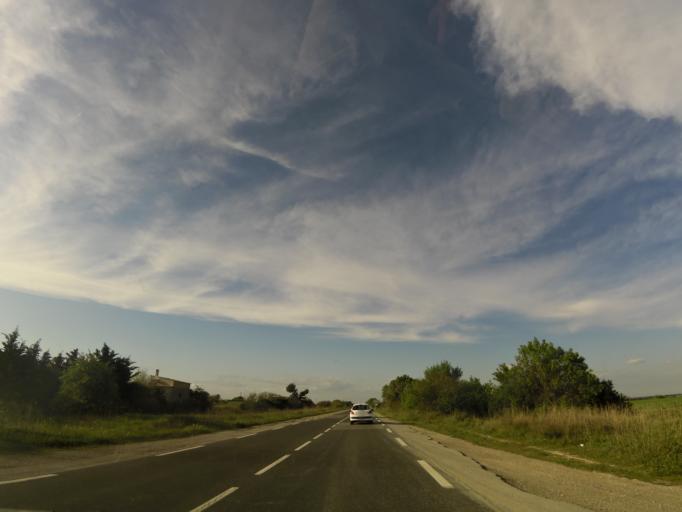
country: FR
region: Languedoc-Roussillon
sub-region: Departement de l'Herault
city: La Grande-Motte
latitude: 43.5941
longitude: 4.1050
